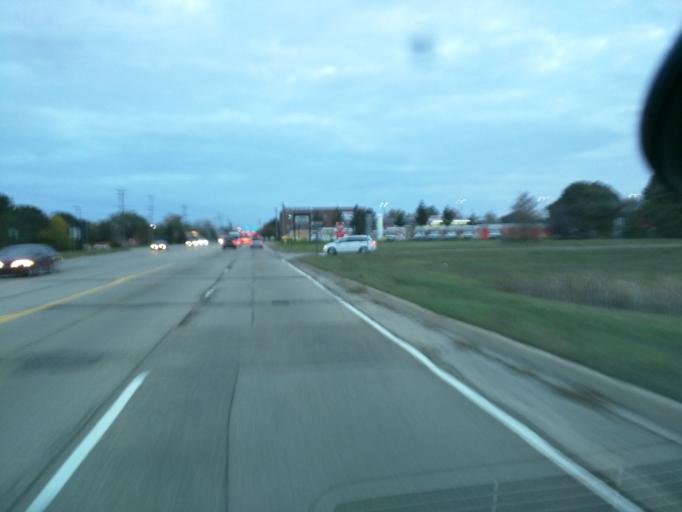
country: US
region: Michigan
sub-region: Eaton County
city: Waverly
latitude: 42.7233
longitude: -84.6029
